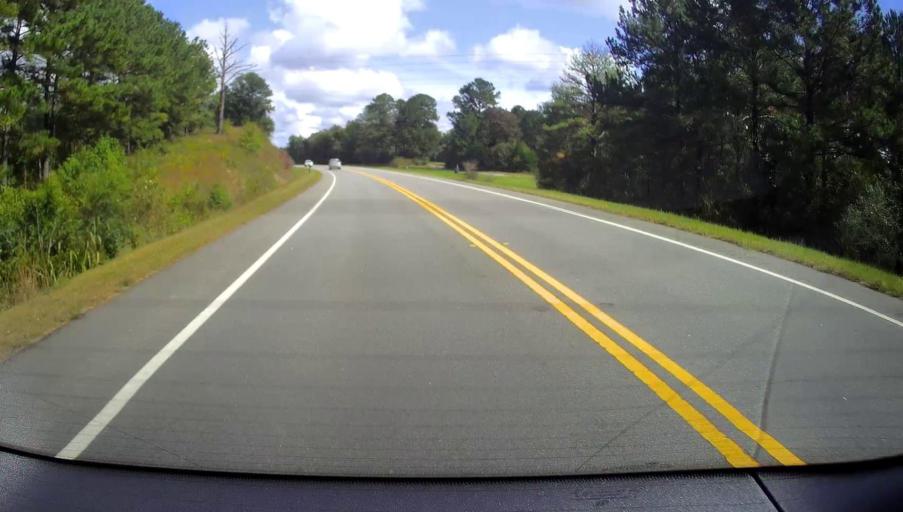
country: US
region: Georgia
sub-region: Baldwin County
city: Milledgeville
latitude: 33.0732
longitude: -83.3213
